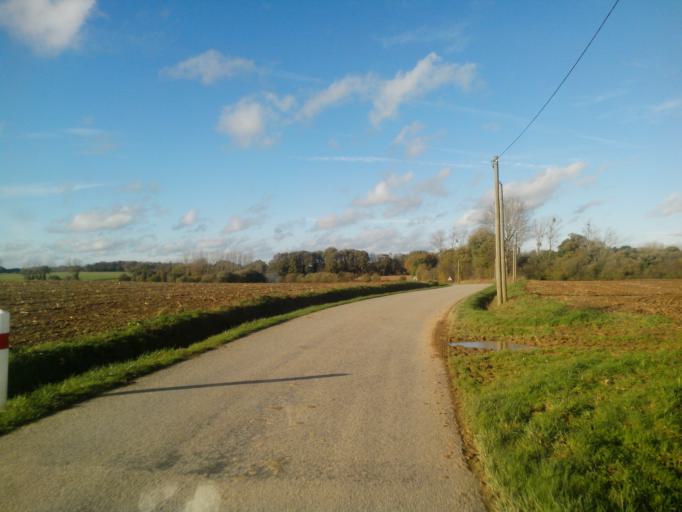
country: FR
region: Brittany
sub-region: Departement du Morbihan
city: Guilliers
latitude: 48.0694
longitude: -2.4093
